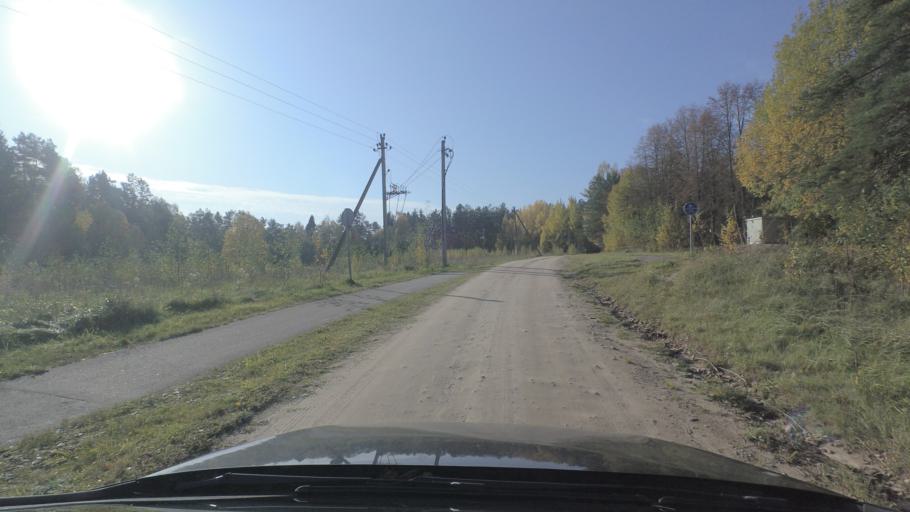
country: LT
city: Ignalina
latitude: 55.3383
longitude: 26.1774
